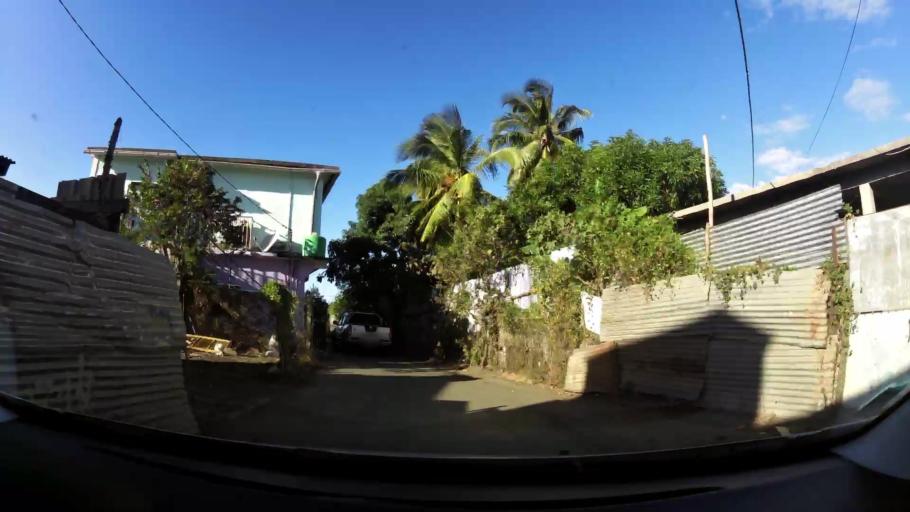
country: YT
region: Koungou
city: Koungou
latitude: -12.7463
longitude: 45.2237
